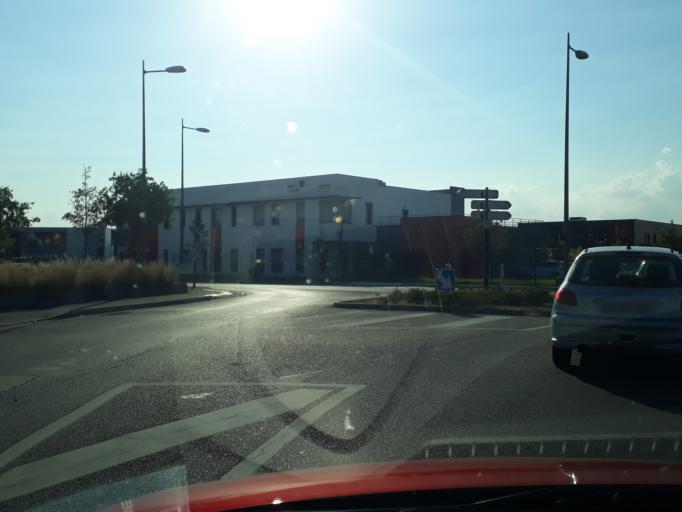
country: FR
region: Rhone-Alpes
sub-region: Departement du Rhone
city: Saint-Priest
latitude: 45.7133
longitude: 4.9570
